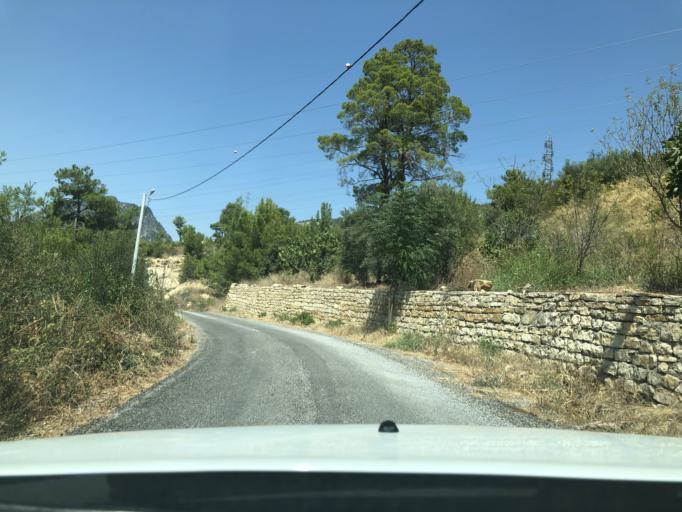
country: TR
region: Antalya
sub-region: Manavgat
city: Manavgat
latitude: 36.8753
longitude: 31.5475
